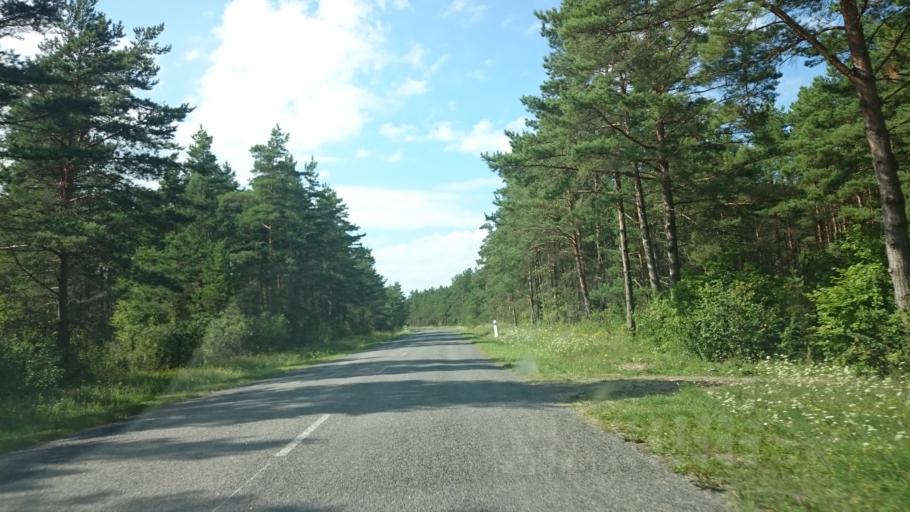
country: EE
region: Saare
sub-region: Orissaare vald
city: Orissaare
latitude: 58.5894
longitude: 23.0169
